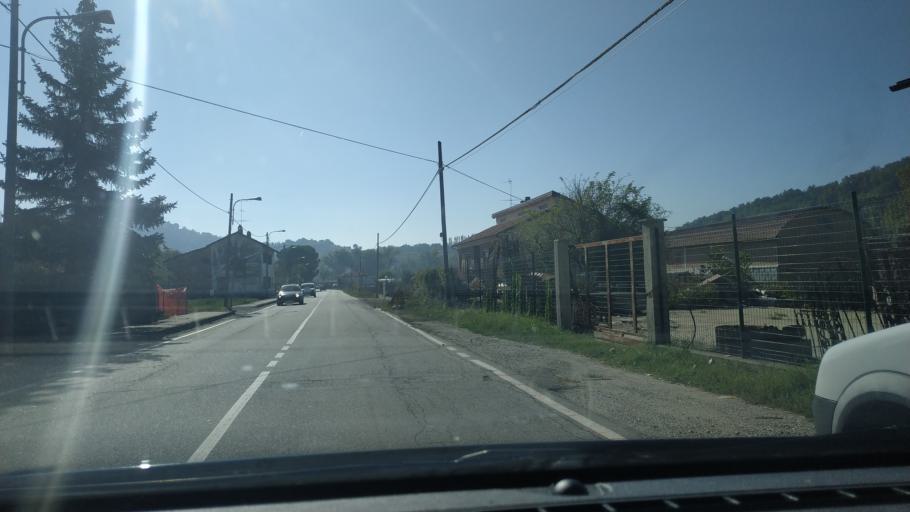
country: IT
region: Piedmont
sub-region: Provincia di Alessandria
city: Murisengo
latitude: 45.0847
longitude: 8.1512
